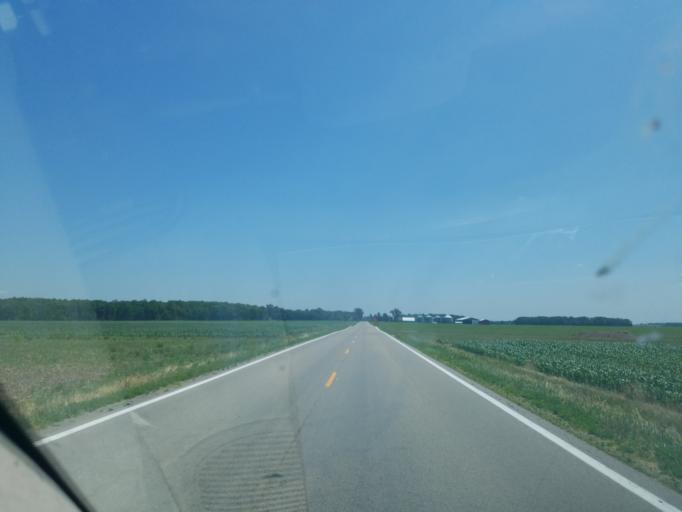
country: US
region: Ohio
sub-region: Allen County
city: Spencerville
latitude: 40.7429
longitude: -84.4265
